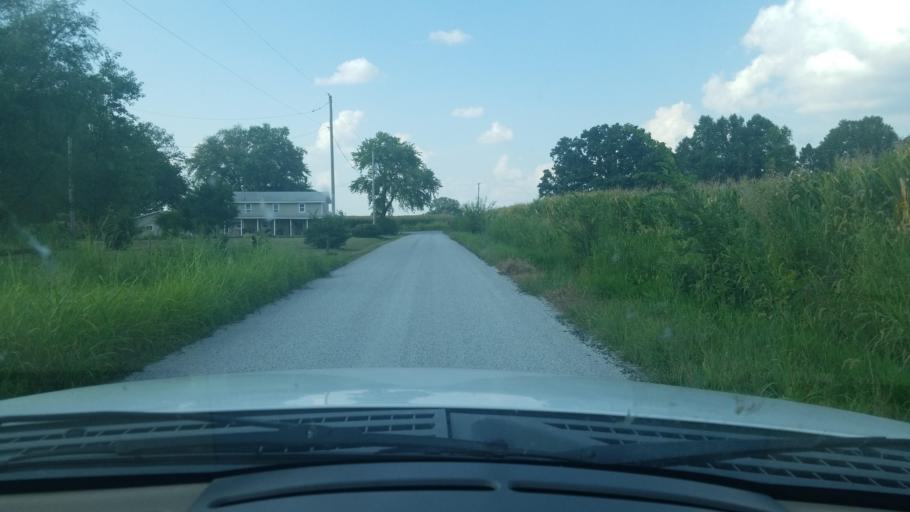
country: US
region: Illinois
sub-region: Saline County
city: Eldorado
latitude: 37.8332
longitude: -88.4386
